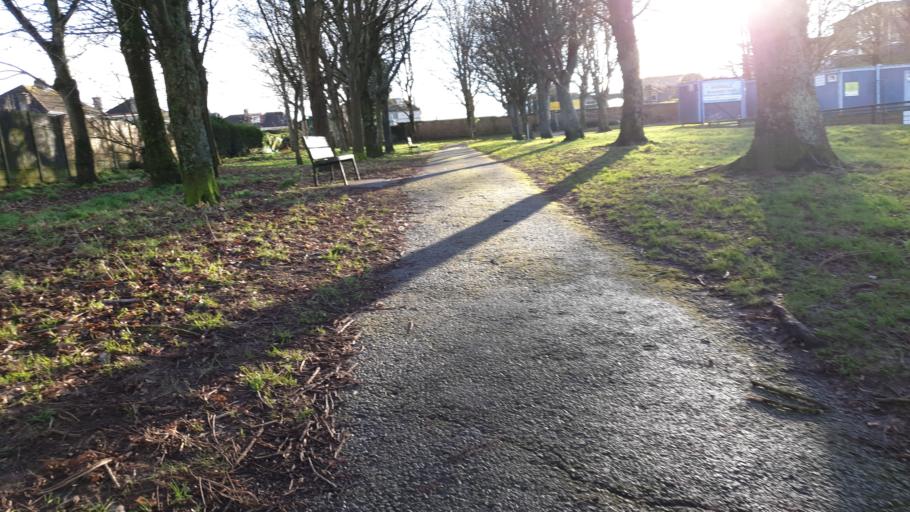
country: IE
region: Munster
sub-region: County Cork
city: Cork
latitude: 51.8904
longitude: -8.4277
